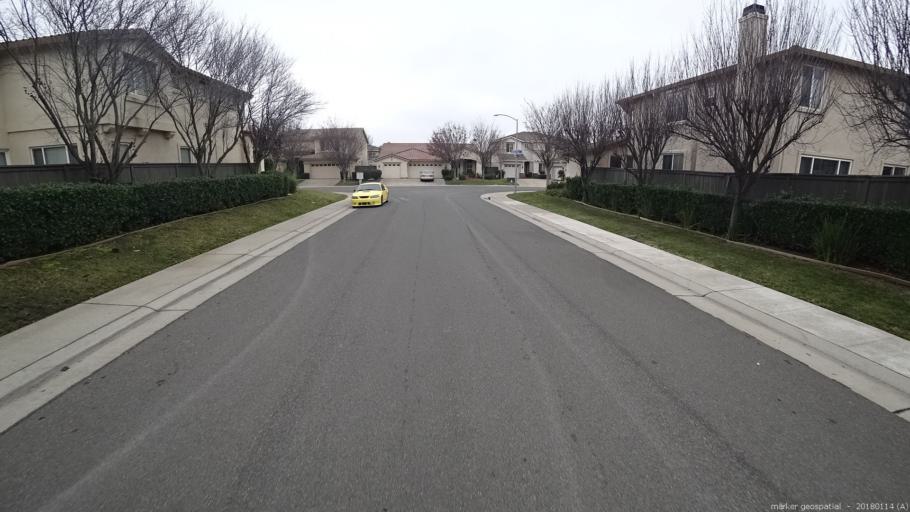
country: US
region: California
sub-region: Sacramento County
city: Gold River
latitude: 38.5535
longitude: -121.2355
